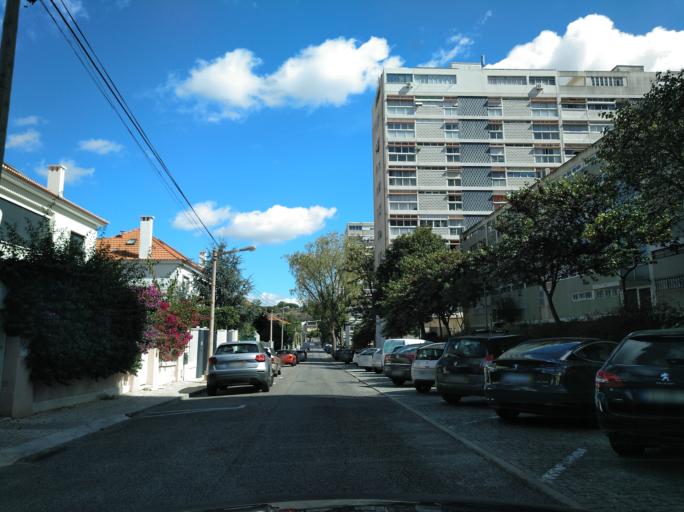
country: PT
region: Lisbon
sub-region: Lisbon
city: Lisbon
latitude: 38.7499
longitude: -9.1362
